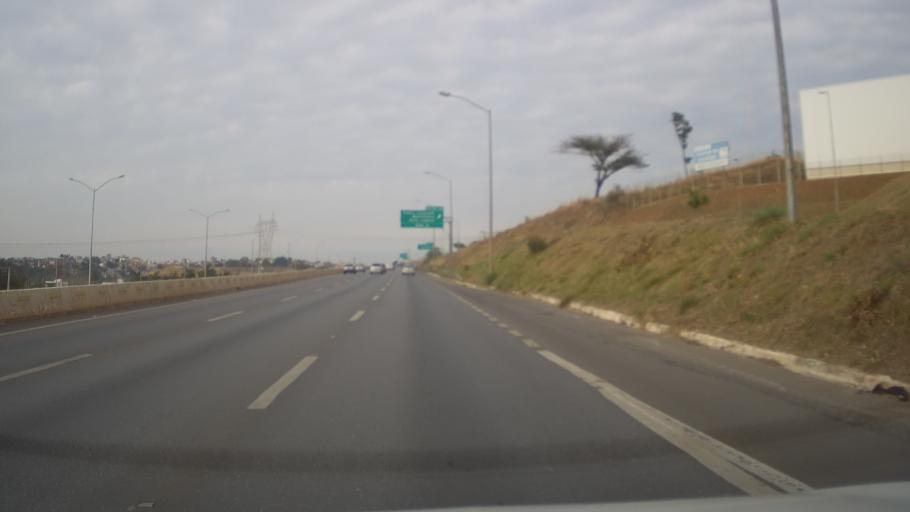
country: BR
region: Minas Gerais
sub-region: Vespasiano
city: Vespasiano
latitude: -19.7349
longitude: -43.9453
